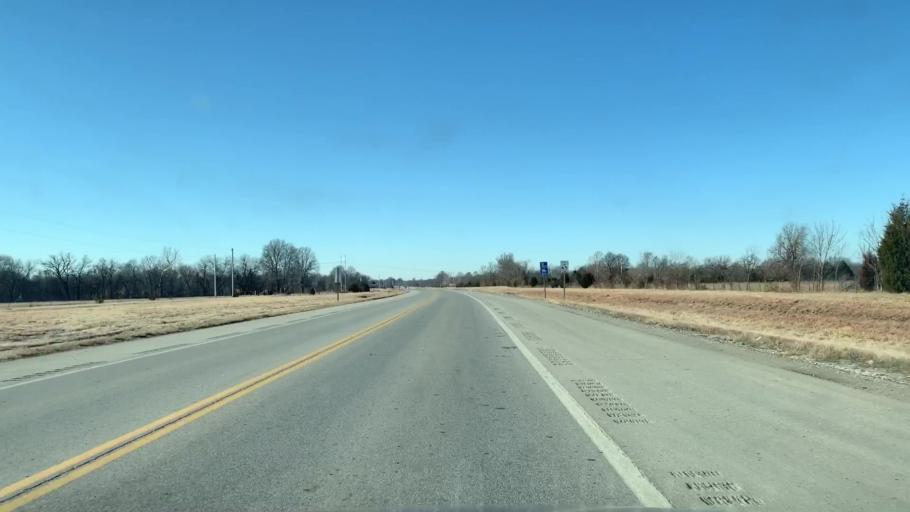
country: US
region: Kansas
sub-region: Cherokee County
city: Baxter Springs
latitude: 37.0737
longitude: -94.7186
